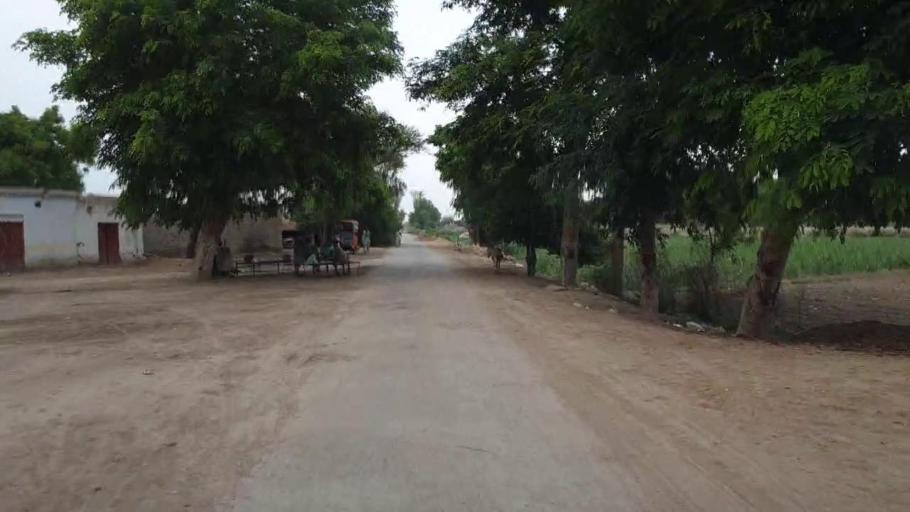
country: PK
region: Sindh
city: Bandhi
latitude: 26.5315
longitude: 68.1992
